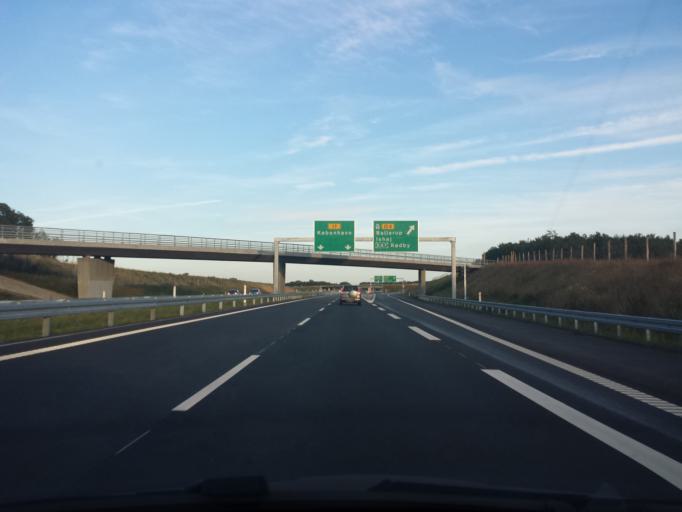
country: DK
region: Capital Region
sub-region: Ballerup Kommune
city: Ballerup
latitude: 55.7069
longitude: 12.3558
